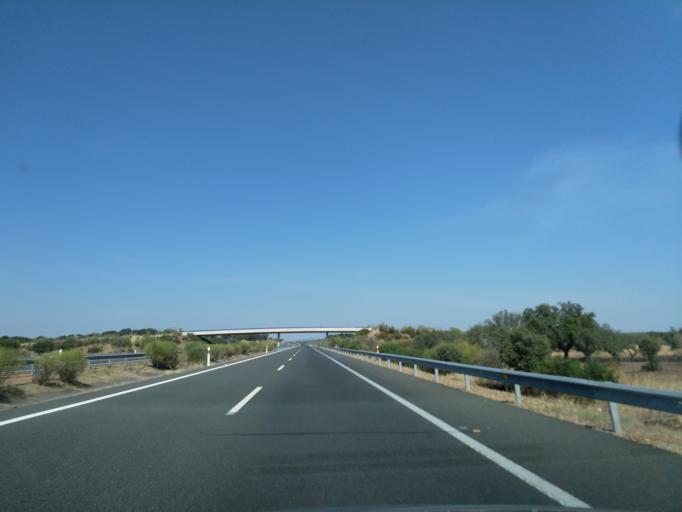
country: ES
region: Extremadura
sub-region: Provincia de Caceres
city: Casas de Don Antonio
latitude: 39.1986
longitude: -6.2798
